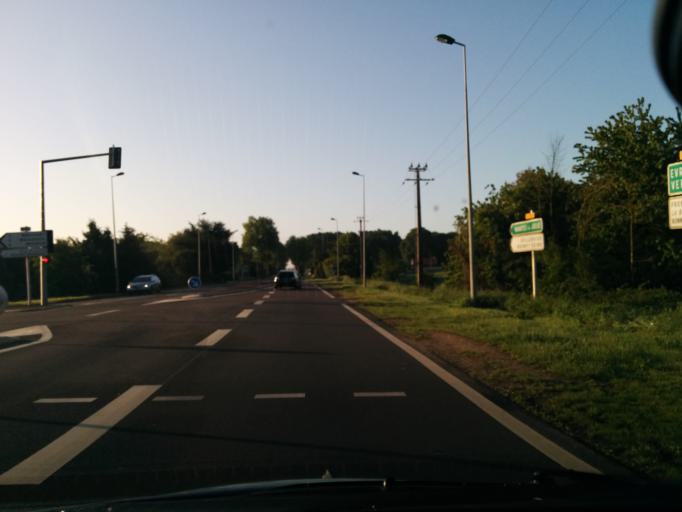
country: FR
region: Ile-de-France
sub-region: Departement des Yvelines
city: Freneuse
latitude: 49.0300
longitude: 1.6063
